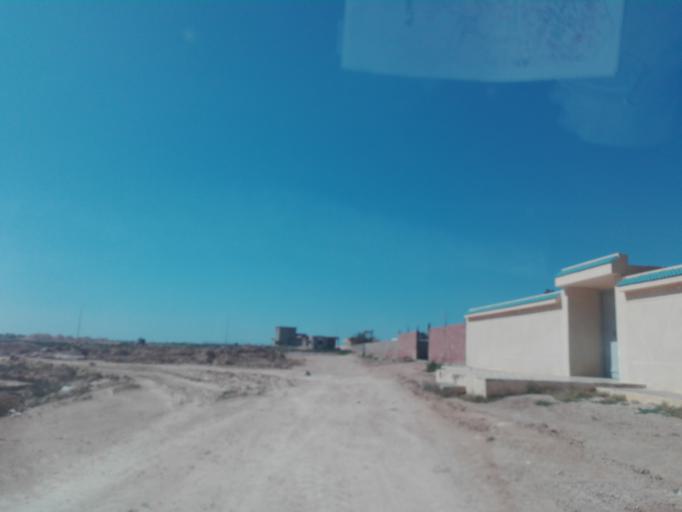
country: TN
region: Safaqis
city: Al Qarmadah
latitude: 34.7037
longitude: 11.1981
